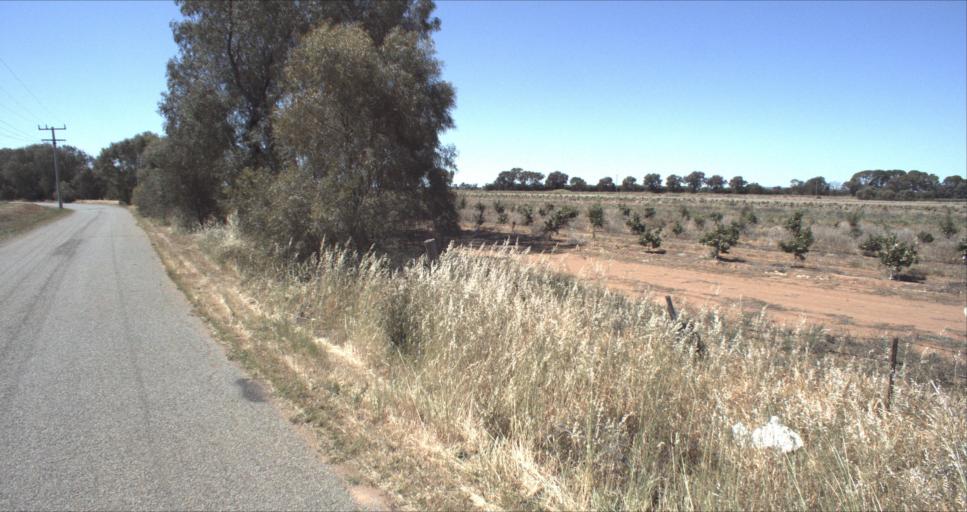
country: AU
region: New South Wales
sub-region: Leeton
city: Leeton
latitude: -34.5276
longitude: 146.3459
